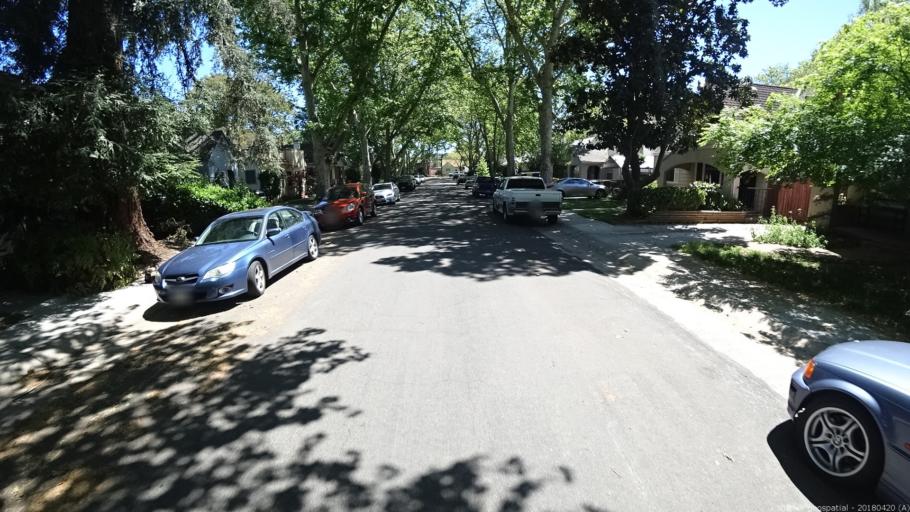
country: US
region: California
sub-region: Sacramento County
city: Sacramento
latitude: 38.5595
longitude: -121.4900
